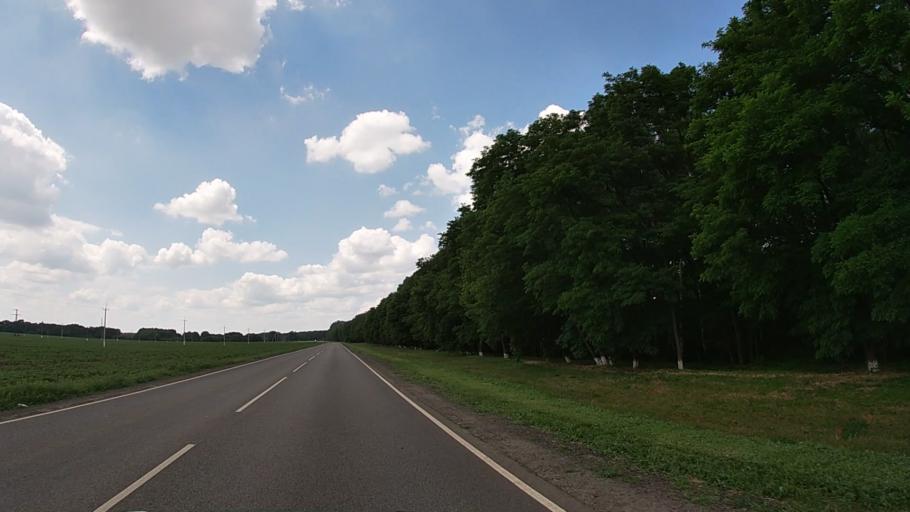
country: RU
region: Belgorod
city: Grayvoron
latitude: 50.5036
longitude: 35.7367
